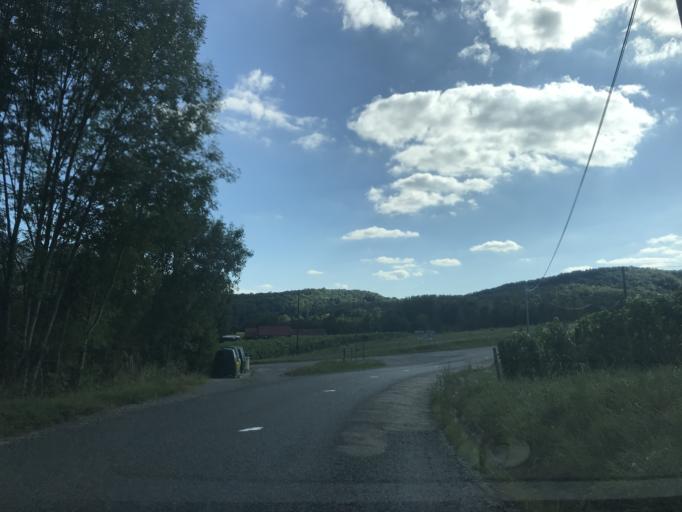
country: FR
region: Rhone-Alpes
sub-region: Departement de la Savoie
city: Yenne
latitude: 45.7168
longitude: 5.8157
